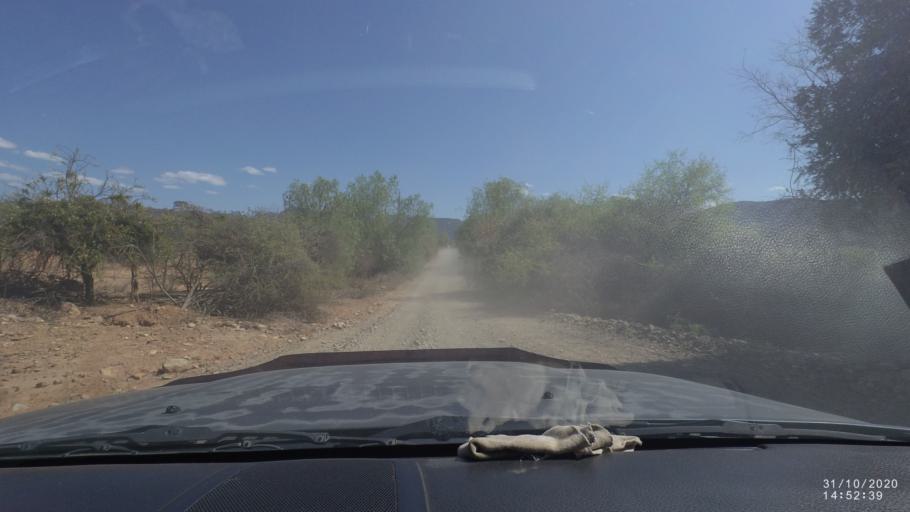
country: BO
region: Cochabamba
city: Aiquile
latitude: -18.2150
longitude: -64.8568
